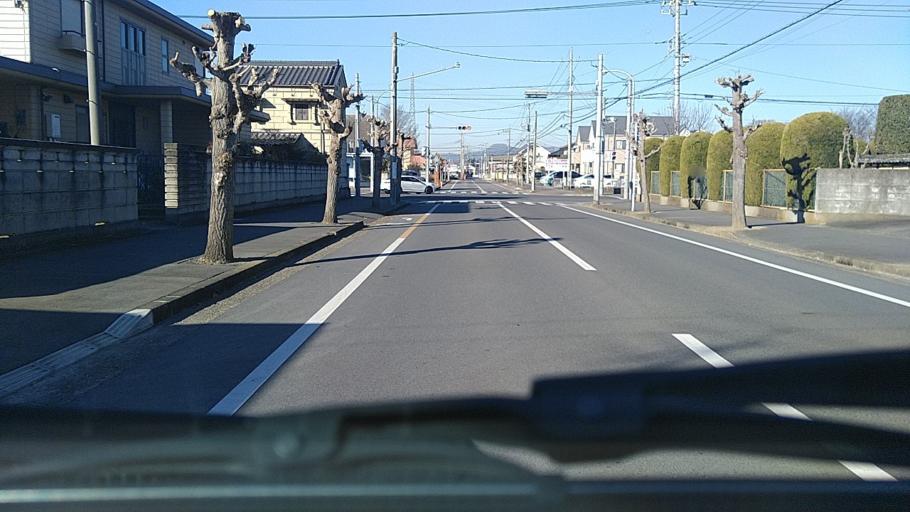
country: JP
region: Tochigi
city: Tanuma
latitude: 36.3455
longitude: 139.5772
